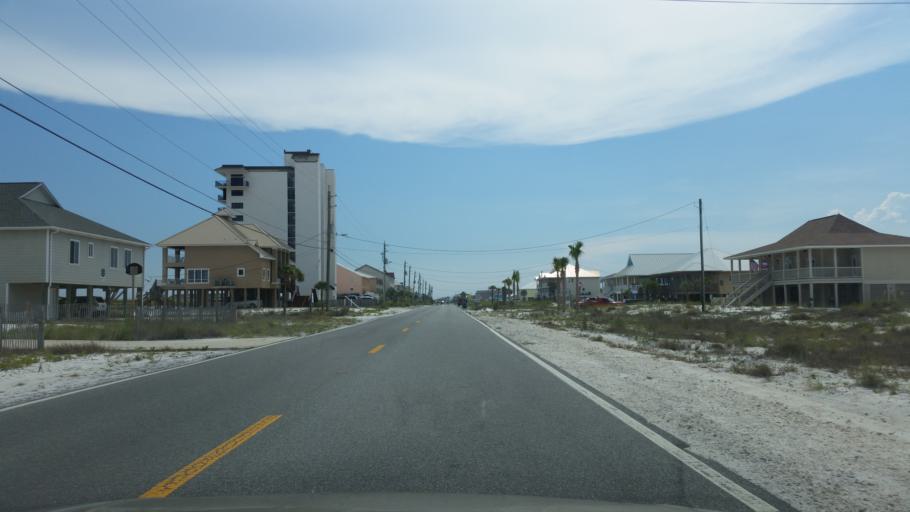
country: US
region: Florida
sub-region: Santa Rosa County
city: Navarre
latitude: 30.3767
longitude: -86.8882
